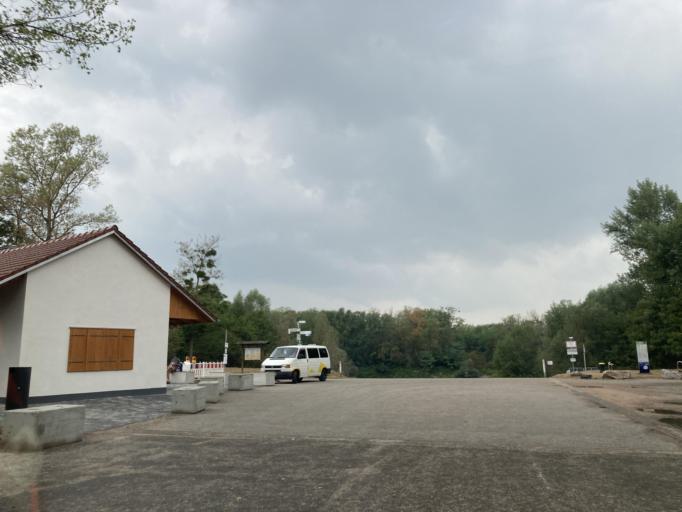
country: FR
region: Alsace
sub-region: Departement du Haut-Rhin
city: Blodelsheim
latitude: 47.8804
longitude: 7.5603
